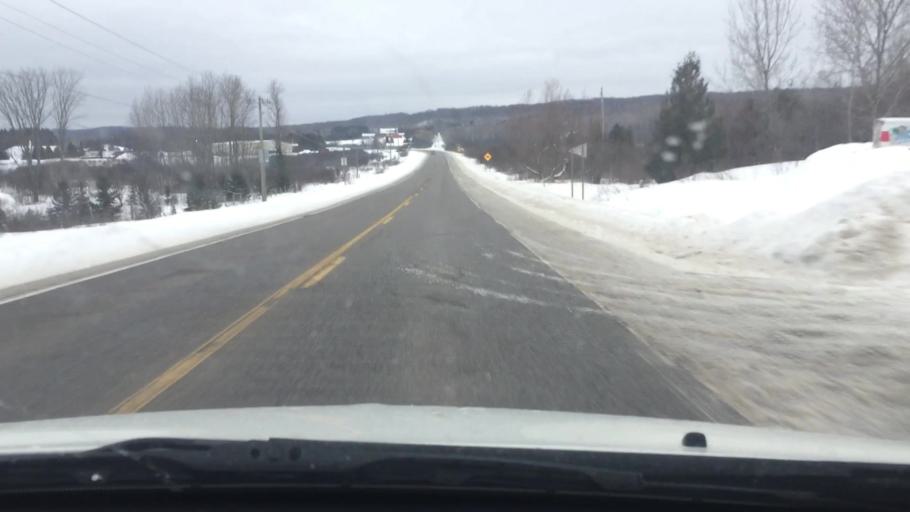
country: US
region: Michigan
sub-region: Charlevoix County
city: East Jordan
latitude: 45.1376
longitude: -85.1398
